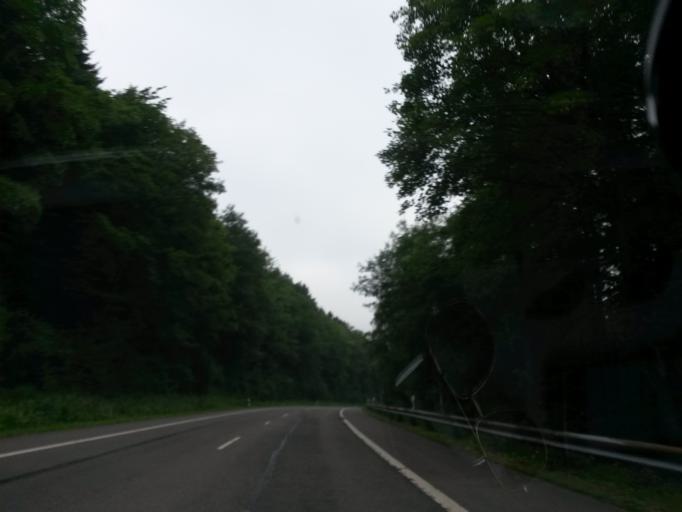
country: DE
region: North Rhine-Westphalia
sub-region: Regierungsbezirk Koln
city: Engelskirchen
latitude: 50.9784
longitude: 7.4345
